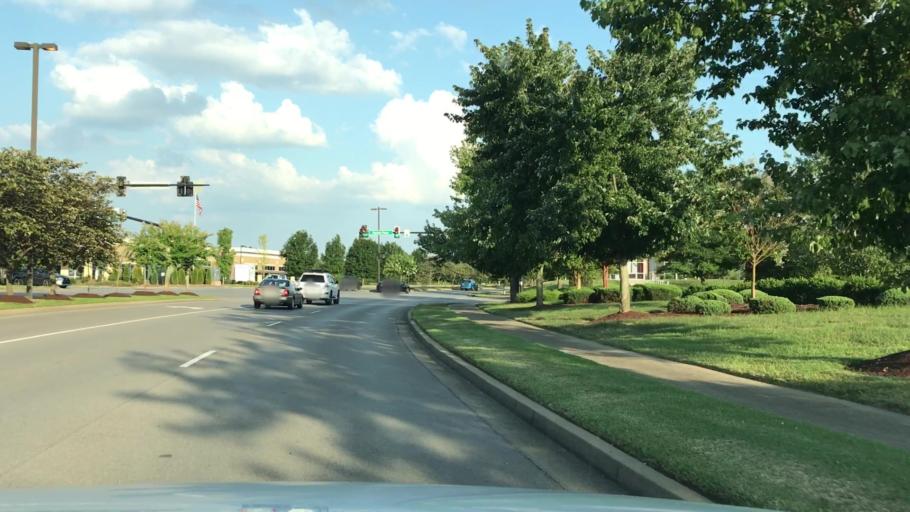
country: US
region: Tennessee
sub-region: Sumner County
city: Hendersonville
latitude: 36.3200
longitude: -86.5972
